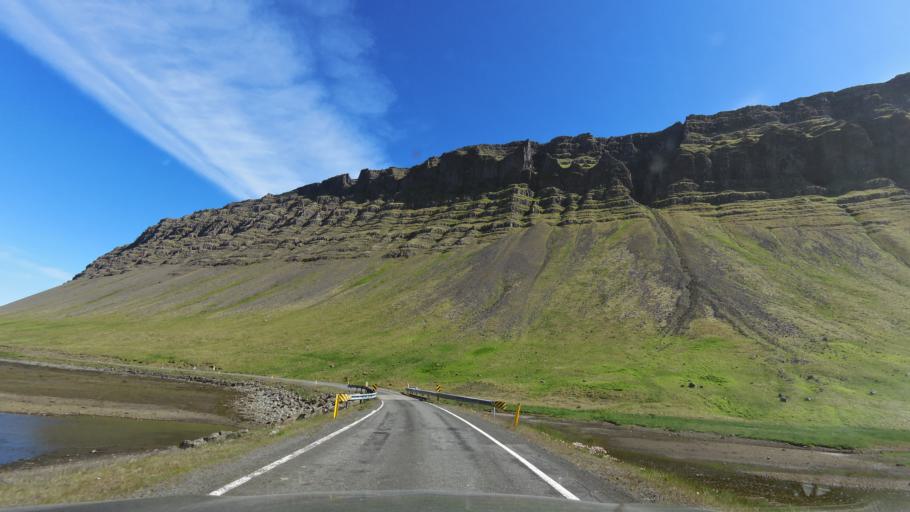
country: IS
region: Westfjords
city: Isafjoerdur
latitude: 65.6740
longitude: -23.6054
